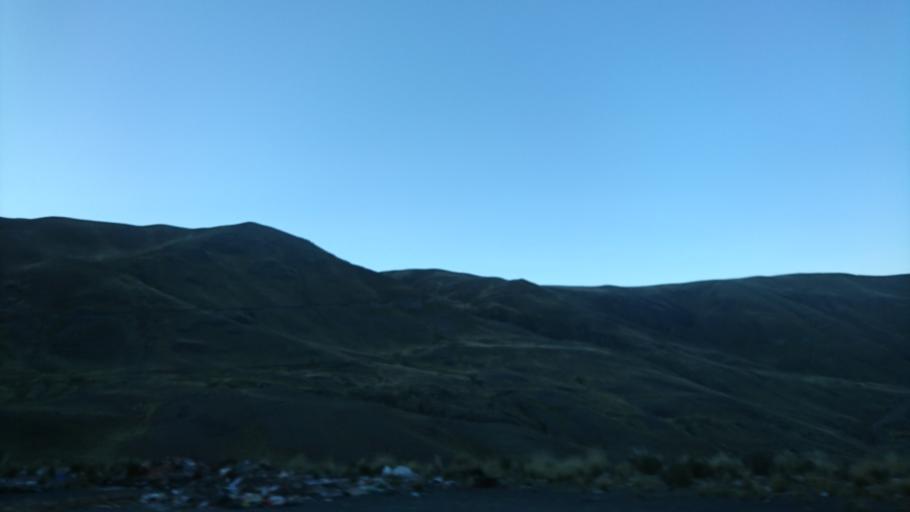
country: BO
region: La Paz
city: La Paz
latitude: -16.4127
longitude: -68.0523
